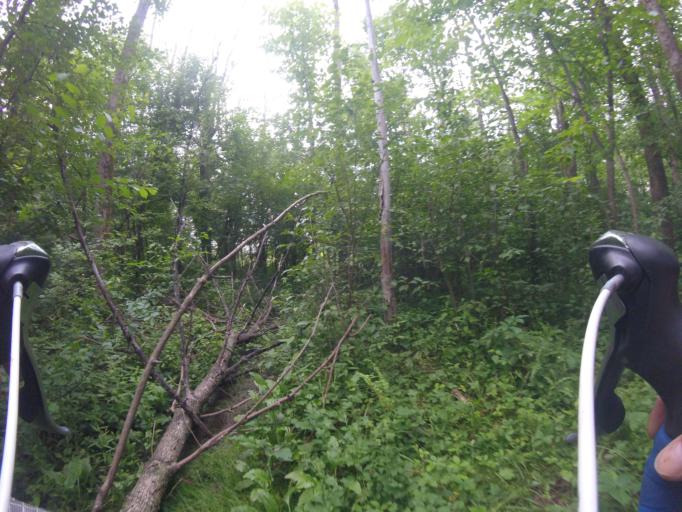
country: CA
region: Ontario
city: Bells Corners
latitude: 45.3316
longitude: -75.8032
